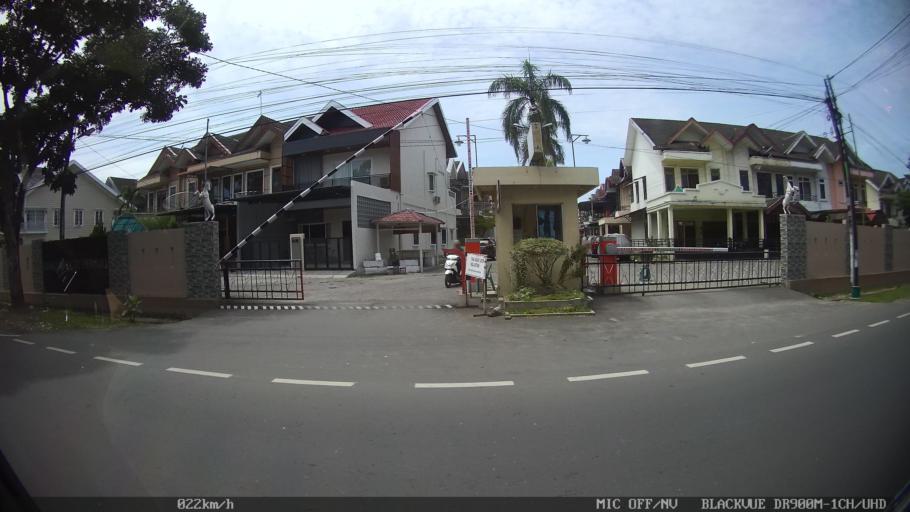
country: ID
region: North Sumatra
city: Sunggal
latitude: 3.5759
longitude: 98.6160
